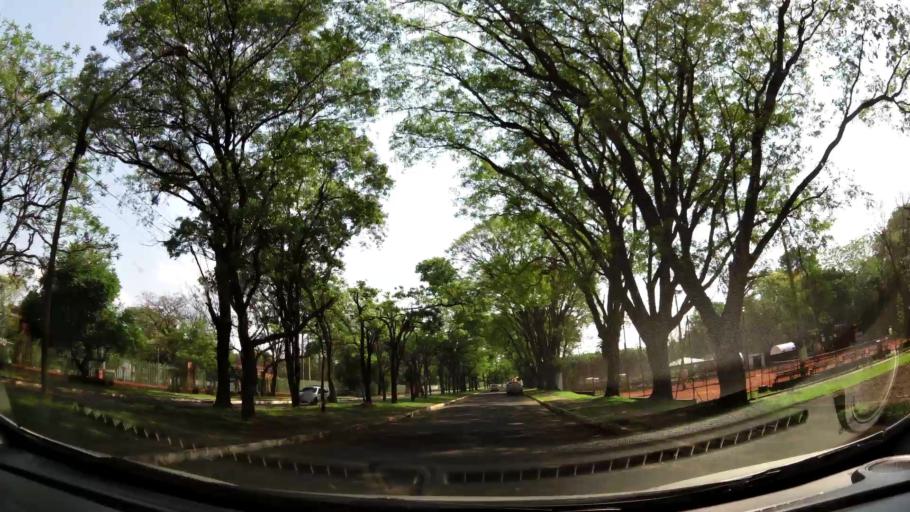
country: PY
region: Alto Parana
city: Presidente Franco
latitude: -25.5186
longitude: -54.6321
